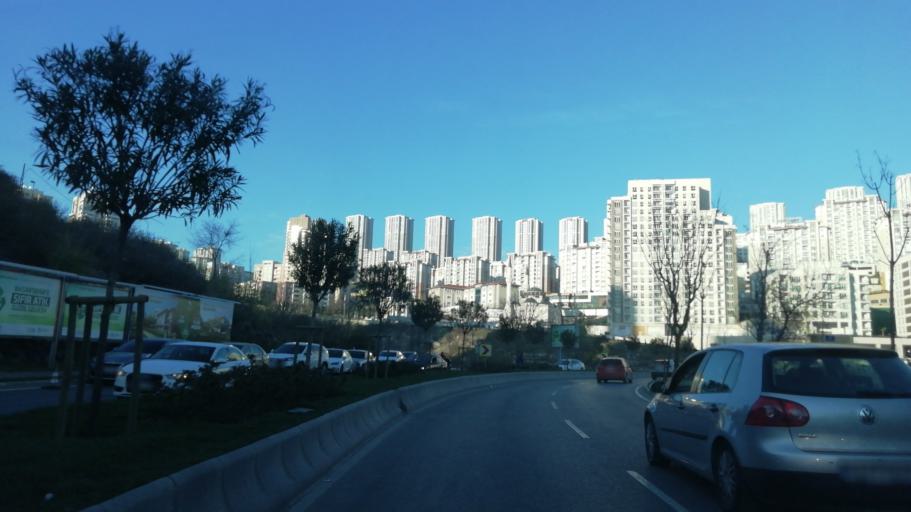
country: TR
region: Istanbul
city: Esenyurt
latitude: 41.0724
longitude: 28.6896
